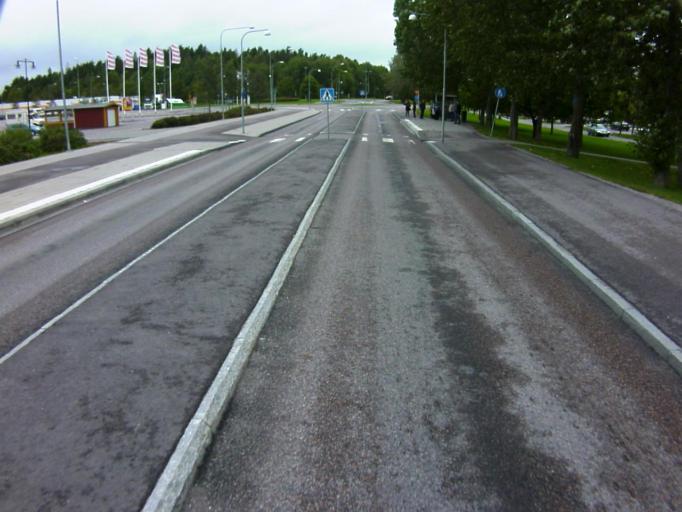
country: SE
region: Soedermanland
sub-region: Eskilstuna Kommun
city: Eskilstuna
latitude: 59.3890
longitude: 16.5354
